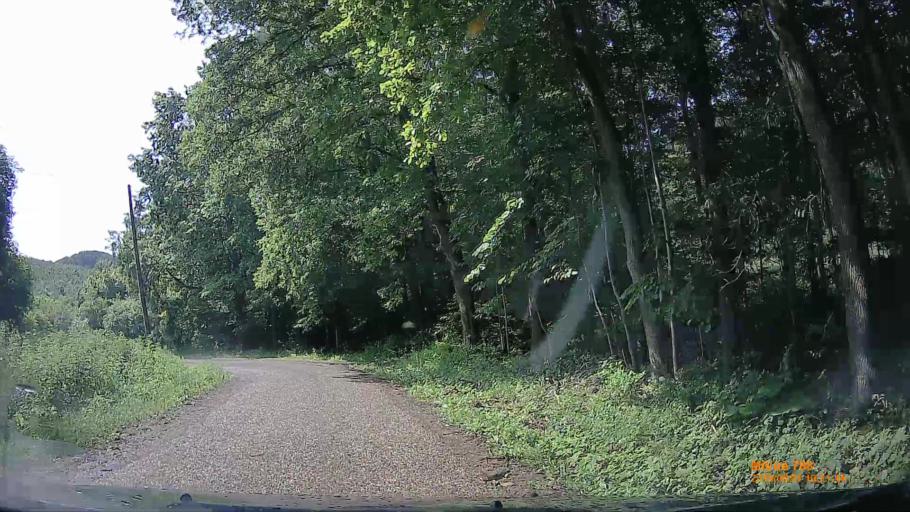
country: HU
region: Baranya
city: Buekkoesd
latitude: 46.1958
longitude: 17.9701
